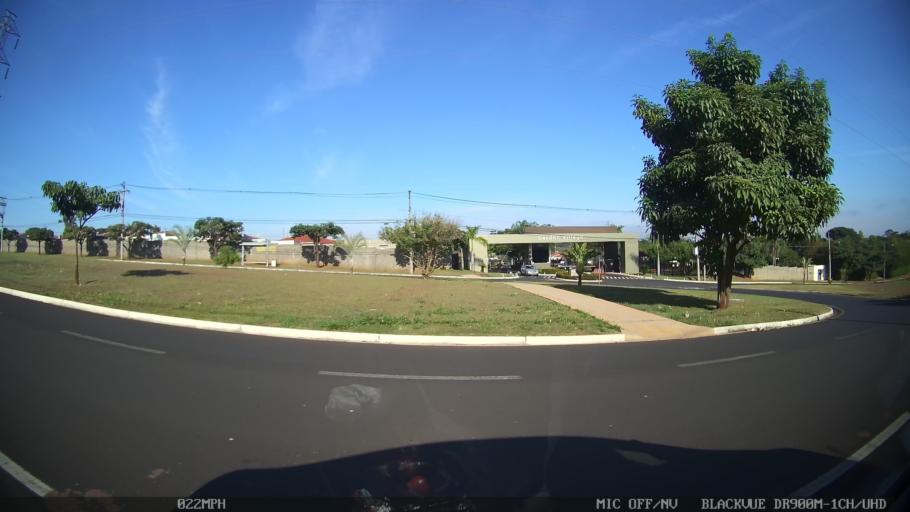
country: BR
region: Sao Paulo
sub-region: Sao Jose Do Rio Preto
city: Sao Jose do Rio Preto
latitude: -20.7744
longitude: -49.3486
